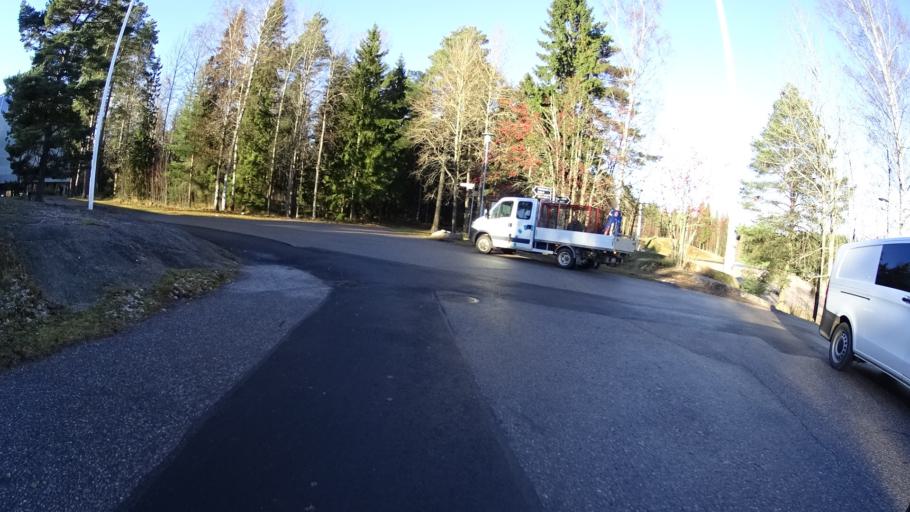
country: FI
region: Uusimaa
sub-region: Helsinki
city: Helsinki
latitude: 60.2325
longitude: 24.9123
